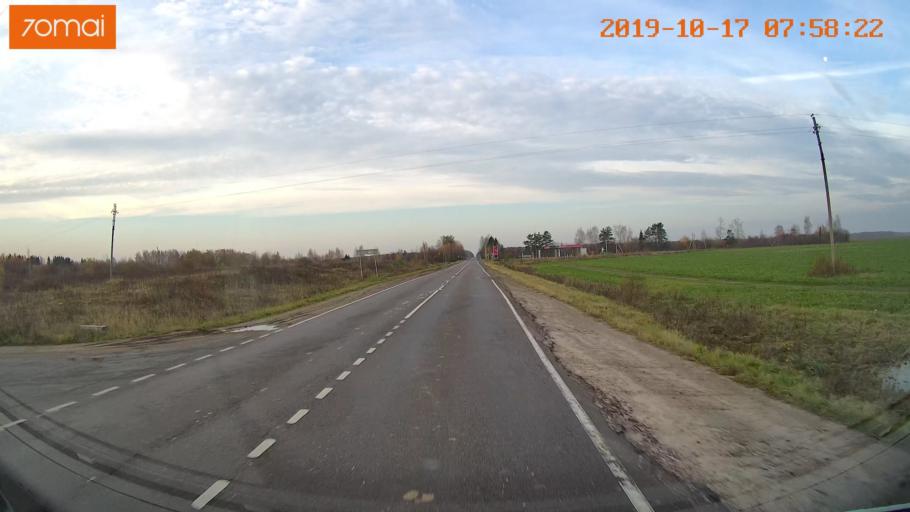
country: RU
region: Vladimir
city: Bavleny
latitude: 56.4033
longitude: 39.5589
